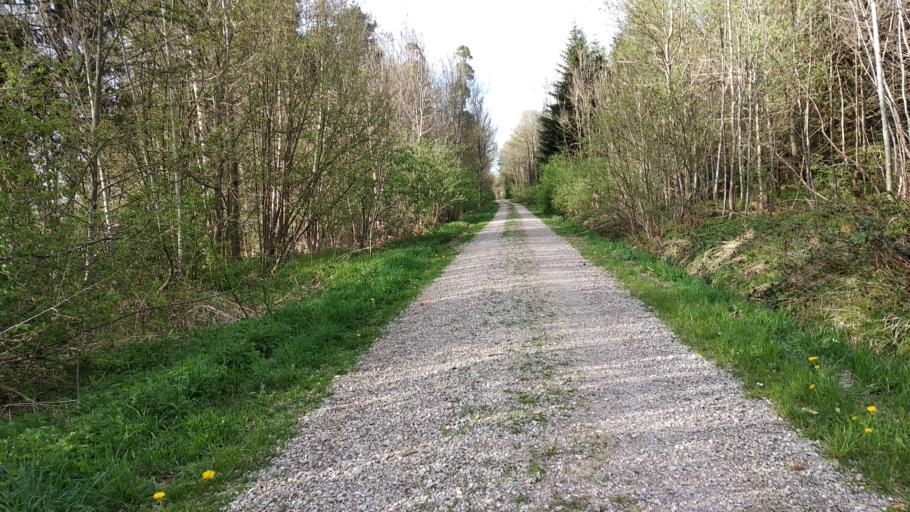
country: DE
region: Bavaria
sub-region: Swabia
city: Woringen
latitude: 47.9325
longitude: 10.1889
